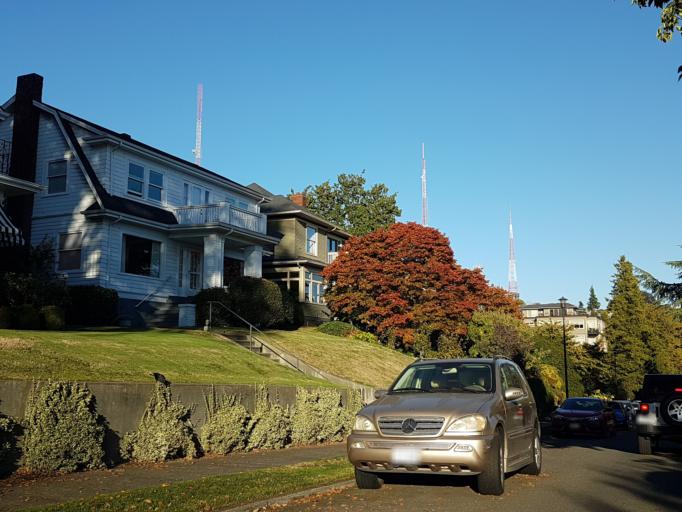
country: US
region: Washington
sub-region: King County
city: Seattle
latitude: 47.6305
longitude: -122.3617
